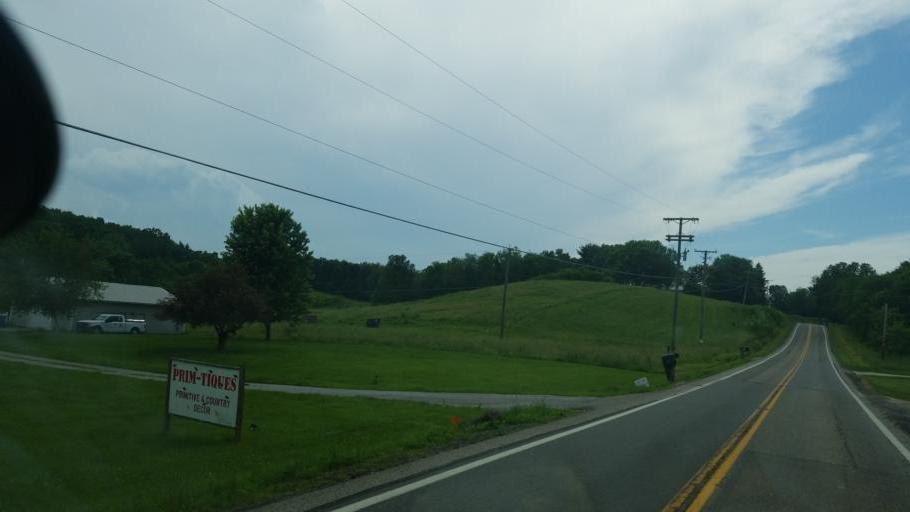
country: US
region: Ohio
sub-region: Knox County
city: Gambier
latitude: 40.2806
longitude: -82.3084
